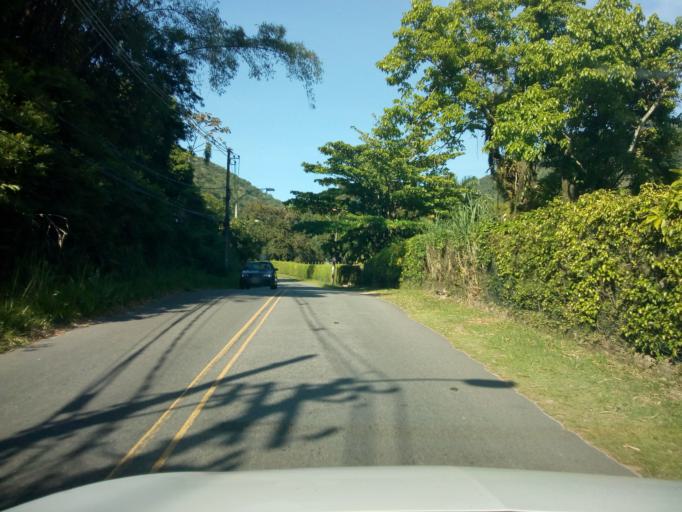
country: BR
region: Rio de Janeiro
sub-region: Nilopolis
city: Nilopolis
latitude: -23.0258
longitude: -43.5141
